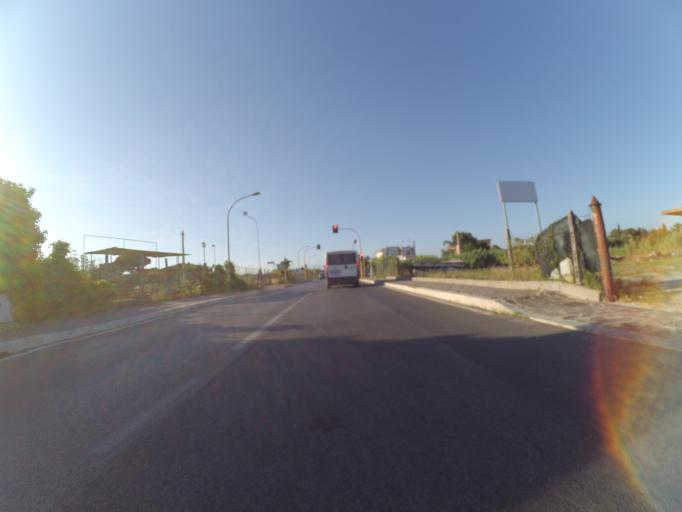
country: IT
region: Latium
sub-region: Provincia di Latina
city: San Felice Circeo
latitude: 41.2519
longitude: 13.0934
